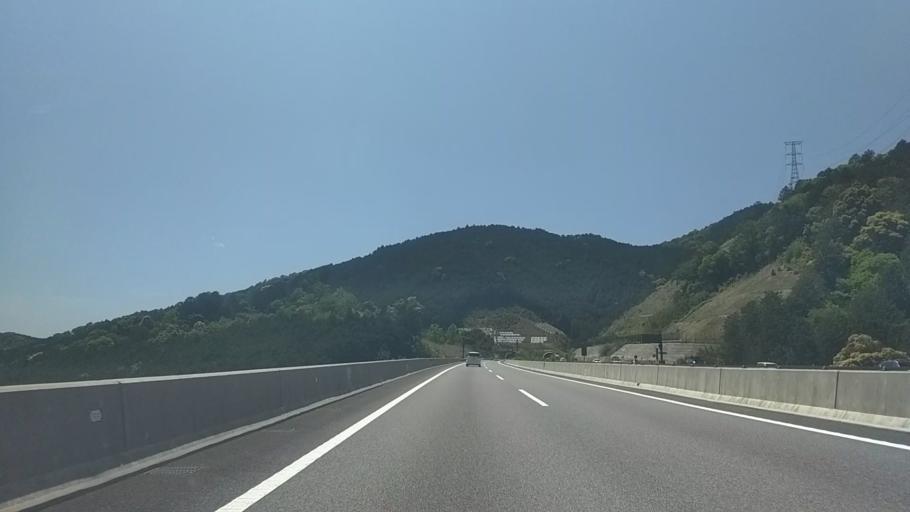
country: JP
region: Aichi
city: Shinshiro
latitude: 34.8978
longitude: 137.4431
